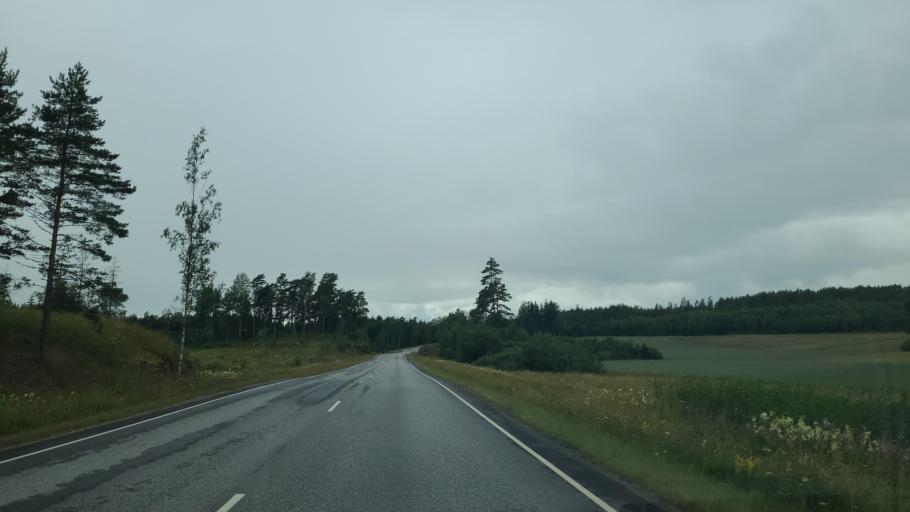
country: FI
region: Varsinais-Suomi
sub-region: Aboland-Turunmaa
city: Kimito
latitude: 60.1913
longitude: 22.6968
